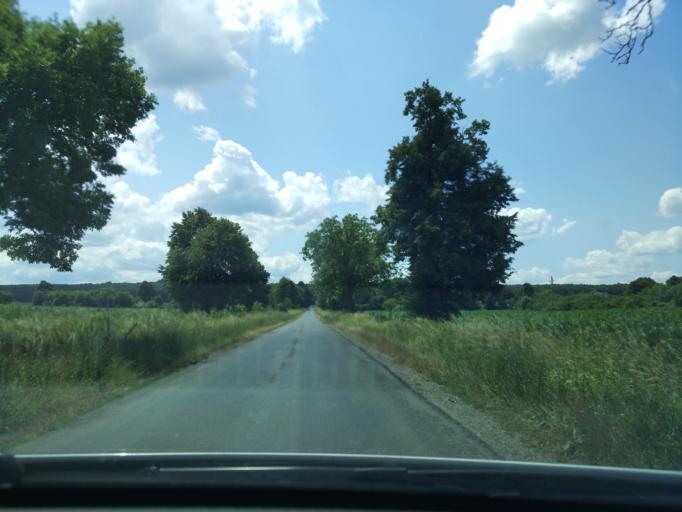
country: HU
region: Veszprem
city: Urkut
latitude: 47.0738
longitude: 17.6842
